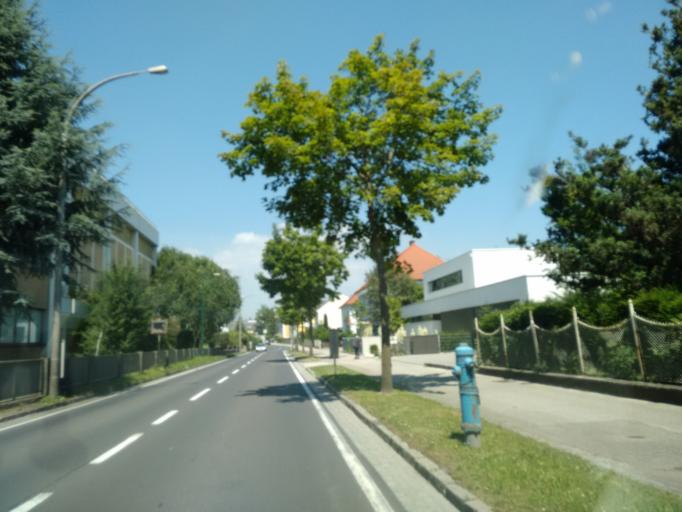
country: AT
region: Upper Austria
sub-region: Politischer Bezirk Urfahr-Umgebung
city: Feldkirchen an der Donau
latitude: 48.3064
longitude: 14.0191
